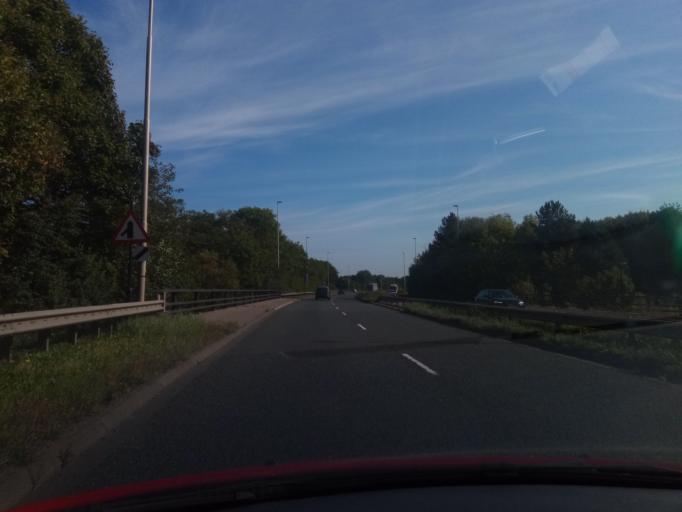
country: GB
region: England
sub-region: Sunderland
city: Washington
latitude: 54.9059
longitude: -1.4884
